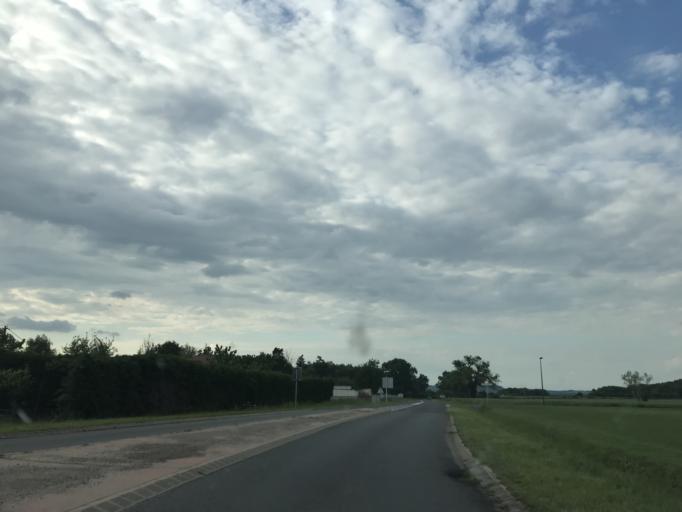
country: FR
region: Auvergne
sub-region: Departement du Puy-de-Dome
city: Maringues
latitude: 45.9071
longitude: 3.3794
